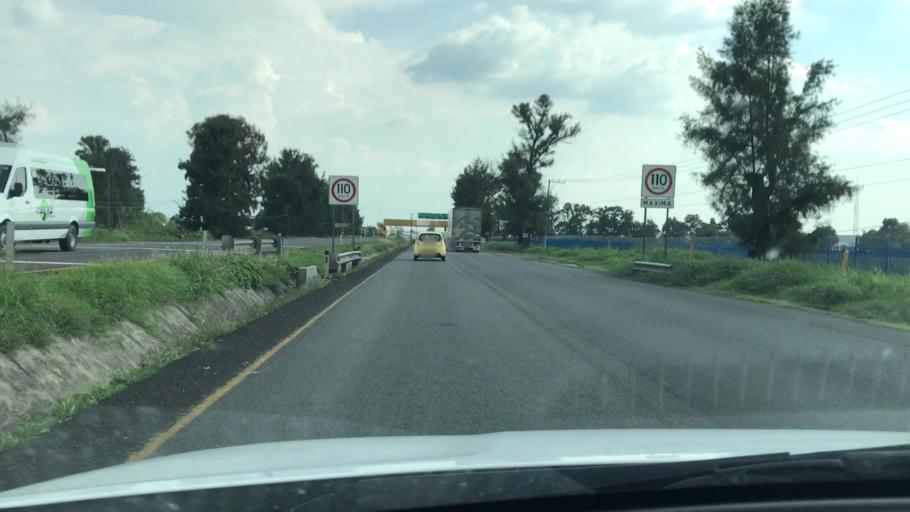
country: MX
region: Guanajuato
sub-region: Irapuato
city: Colonia Morelos de Guadalupe de Rivera
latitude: 20.6005
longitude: -101.4173
